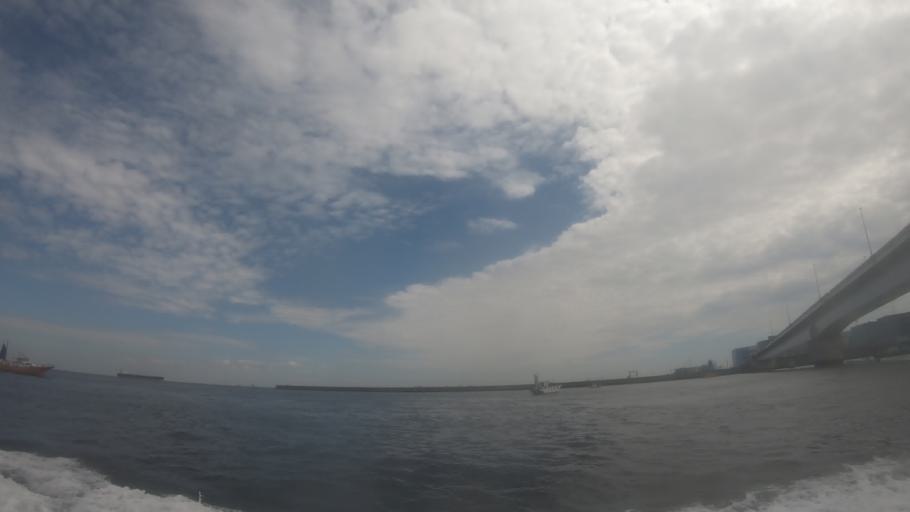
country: JP
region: Kanagawa
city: Yokohama
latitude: 35.4121
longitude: 139.6814
